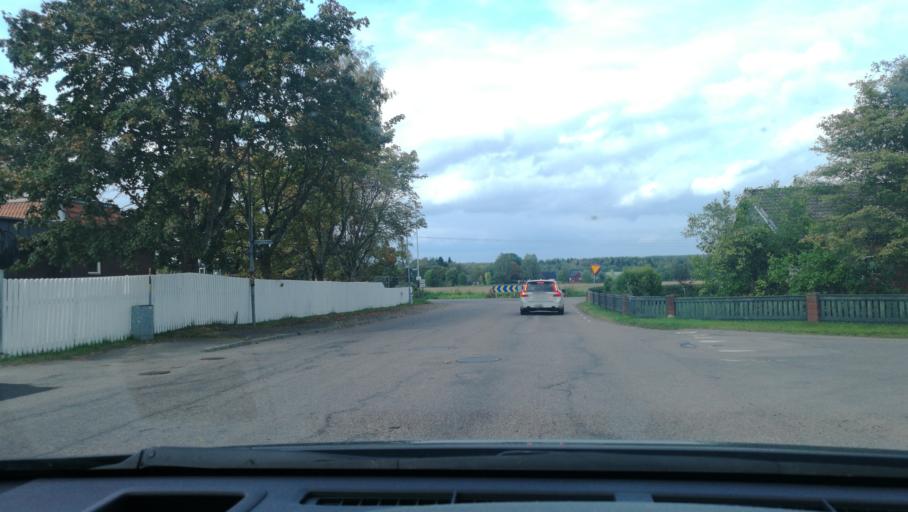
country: SE
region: Dalarna
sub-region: Avesta Kommun
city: Avesta
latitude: 60.1618
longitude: 16.1929
